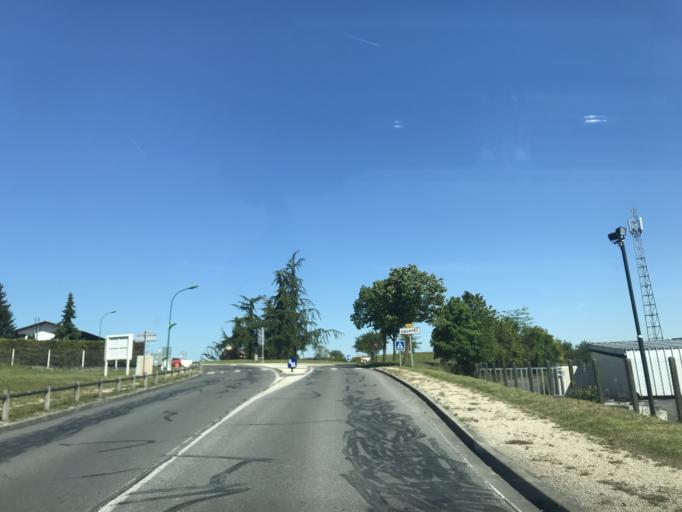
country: FR
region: Poitou-Charentes
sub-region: Departement de la Charente
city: Segonzac
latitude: 45.5279
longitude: -0.3044
